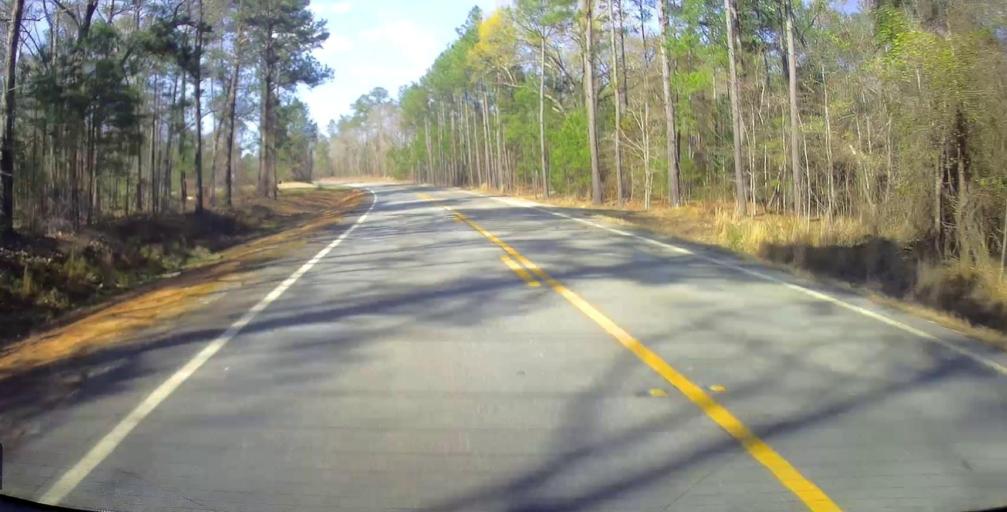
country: US
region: Georgia
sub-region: Wilkinson County
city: Gordon
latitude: 32.8209
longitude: -83.3251
